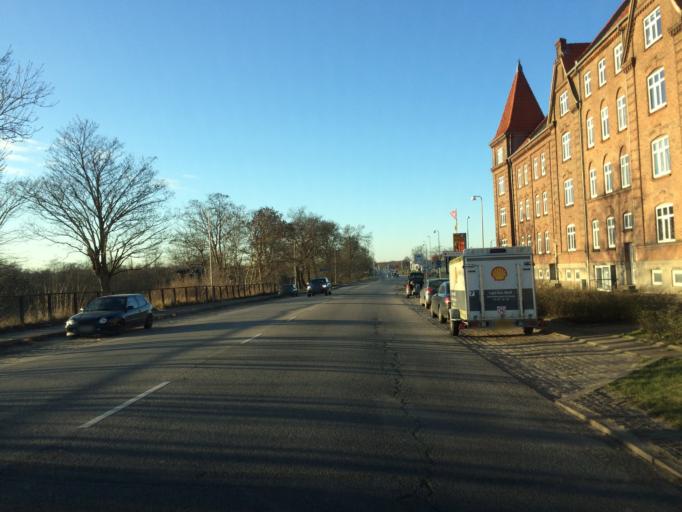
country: DK
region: Central Jutland
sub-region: Randers Kommune
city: Randers
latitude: 56.4630
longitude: 10.0172
